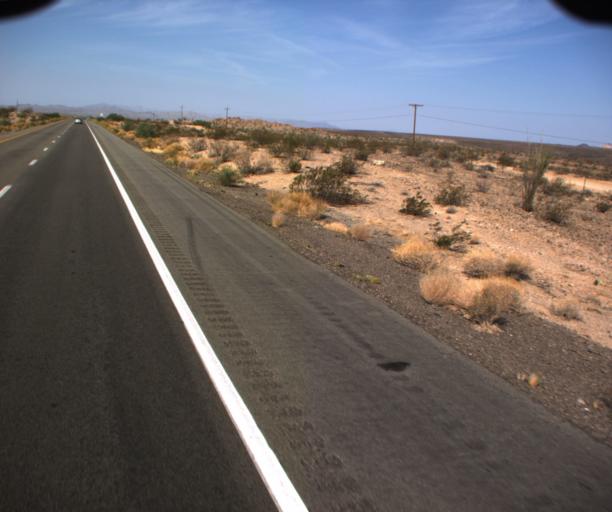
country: US
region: Arizona
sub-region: Mohave County
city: Desert Hills
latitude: 34.7919
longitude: -114.1652
